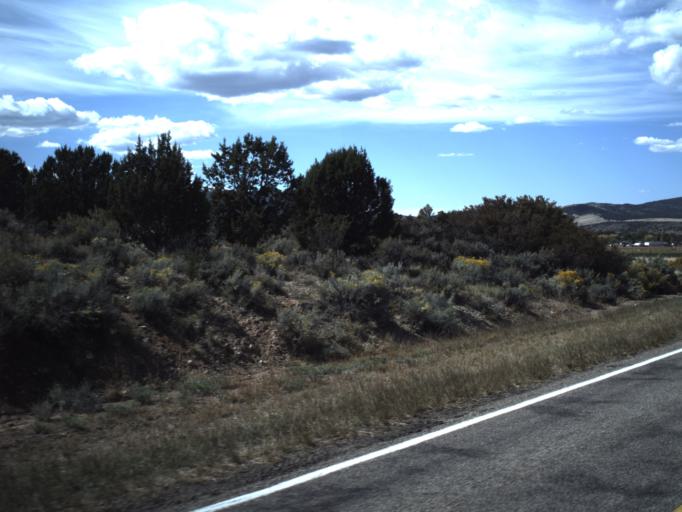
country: US
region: Utah
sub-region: Washington County
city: Enterprise
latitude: 37.5658
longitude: -113.6935
